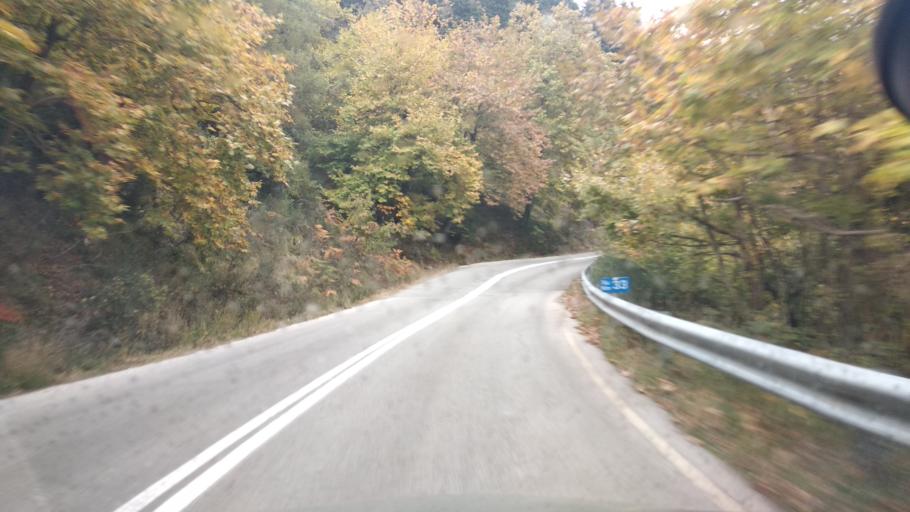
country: GR
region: Thessaly
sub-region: Trikala
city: Pyli
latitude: 39.5099
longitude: 21.5332
